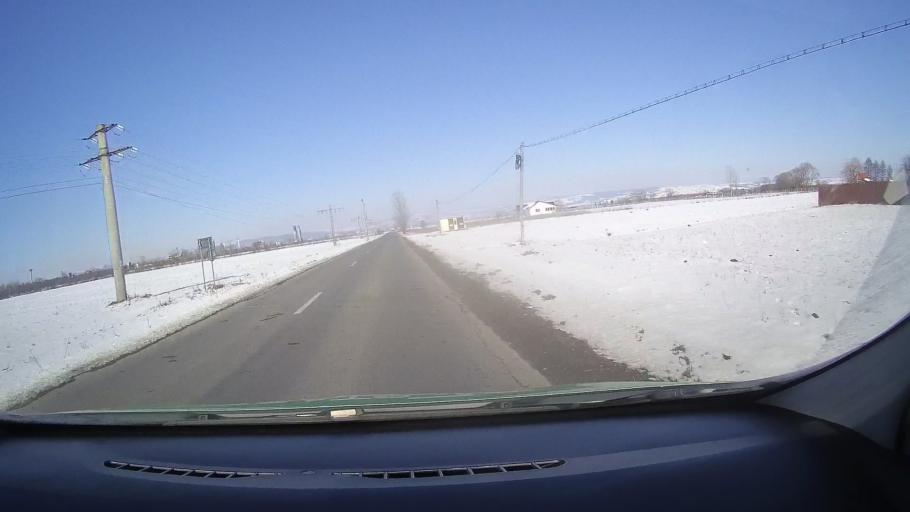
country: RO
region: Brasov
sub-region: Comuna Harseni
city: Harseni
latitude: 45.7951
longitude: 24.9948
